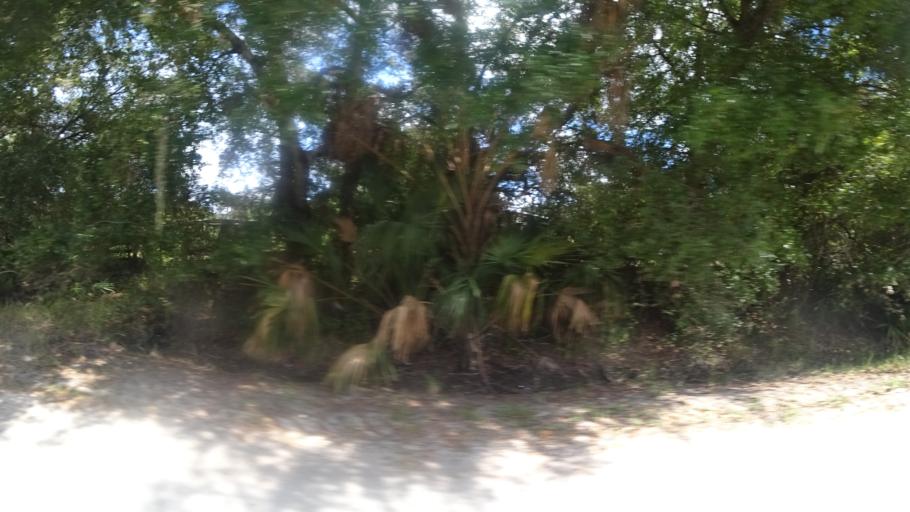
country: US
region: Florida
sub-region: Hillsborough County
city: Sun City Center
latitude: 27.6480
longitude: -82.3593
